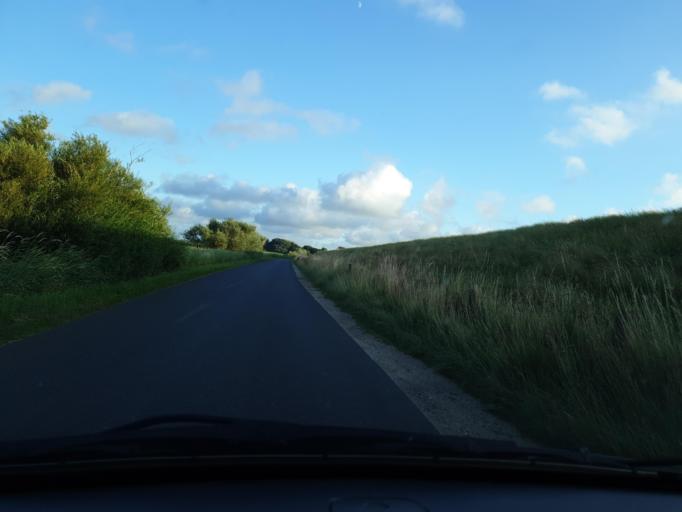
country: DE
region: Schleswig-Holstein
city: Elpersbuttel
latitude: 54.0889
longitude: 9.0317
